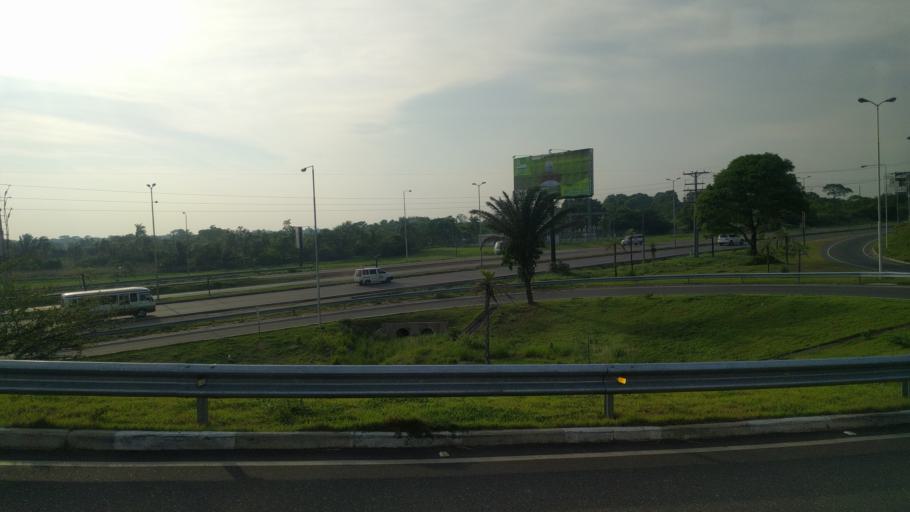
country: BO
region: Santa Cruz
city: La Belgica
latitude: -17.6585
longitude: -63.1587
